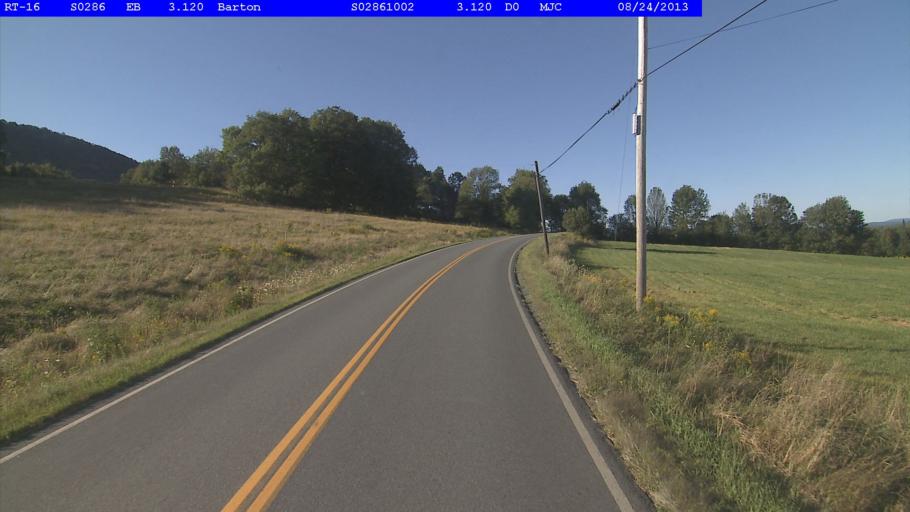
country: US
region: Vermont
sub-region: Orleans County
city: Newport
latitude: 44.7674
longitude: -72.1276
